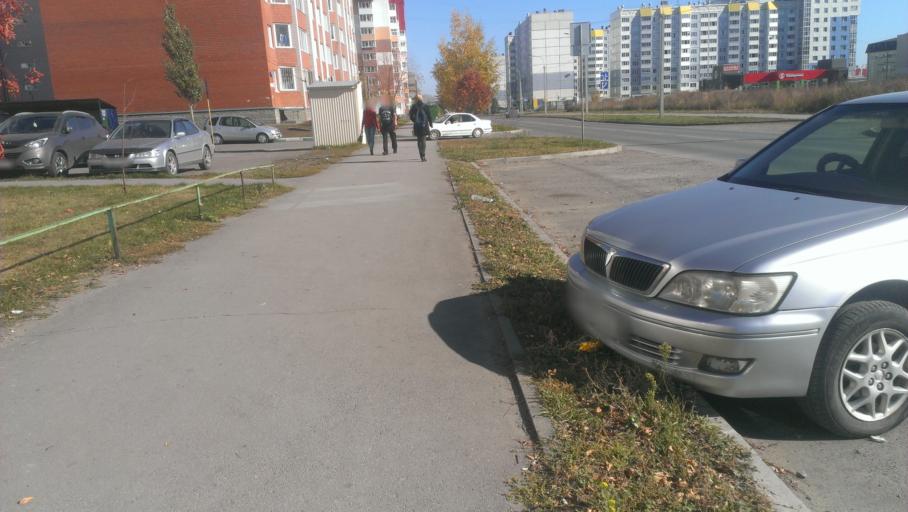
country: RU
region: Altai Krai
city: Novosilikatnyy
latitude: 53.3302
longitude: 83.6819
